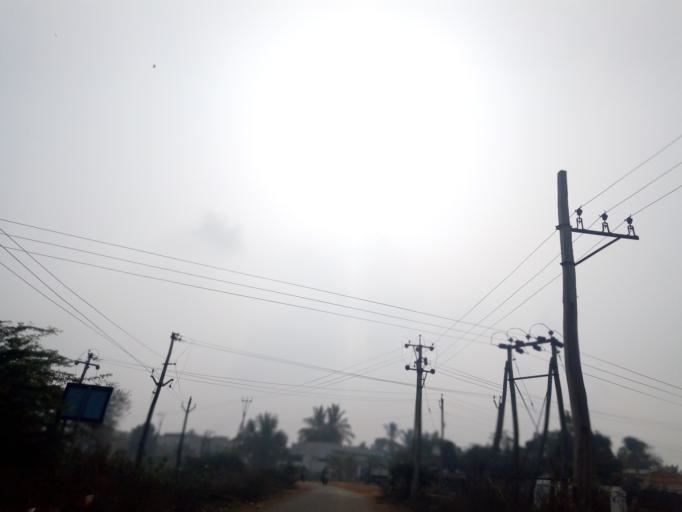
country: IN
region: Andhra Pradesh
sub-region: West Godavari
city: Tadepallegudem
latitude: 16.8378
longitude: 81.3465
